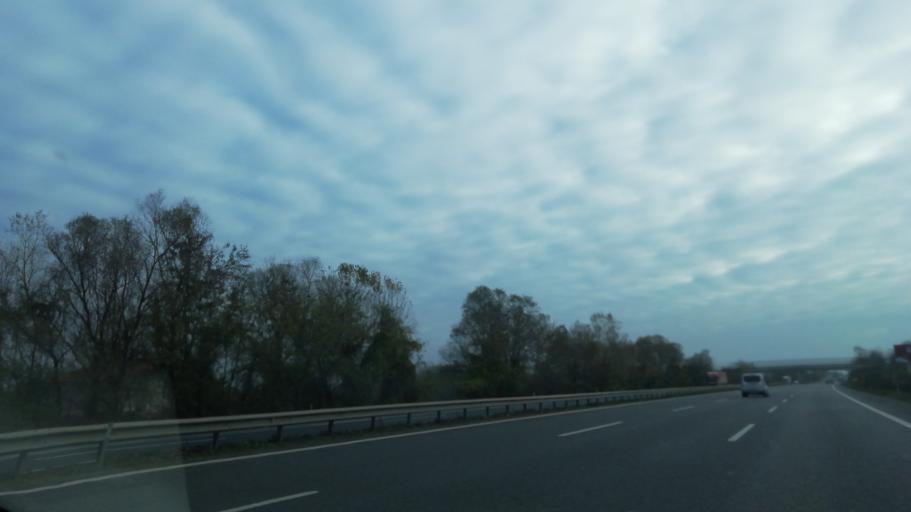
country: TR
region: Sakarya
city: Adapazari
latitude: 40.7187
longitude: 30.4763
